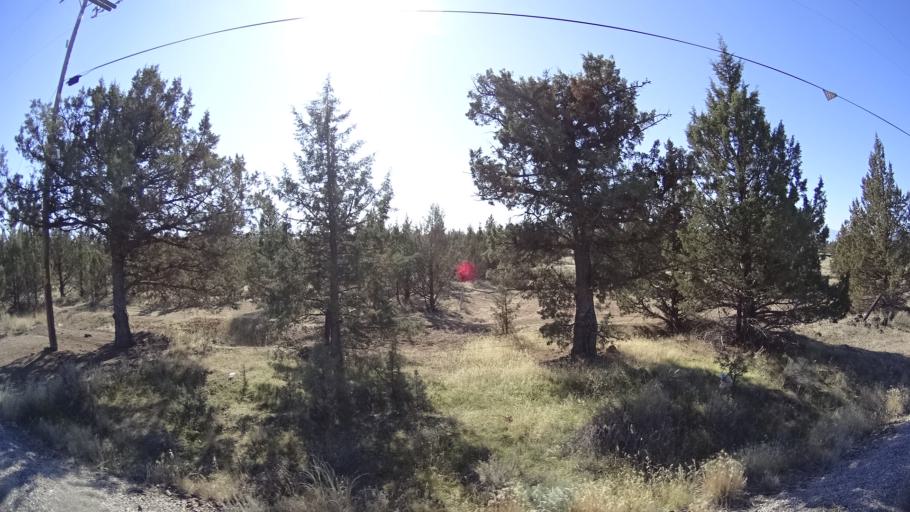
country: US
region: California
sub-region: Siskiyou County
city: Montague
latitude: 41.6599
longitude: -122.3890
